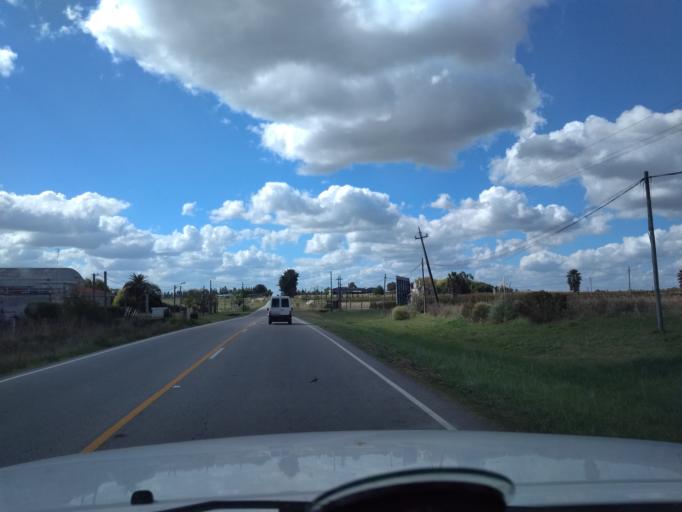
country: UY
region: Canelones
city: Joaquin Suarez
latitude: -34.6922
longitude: -56.0550
